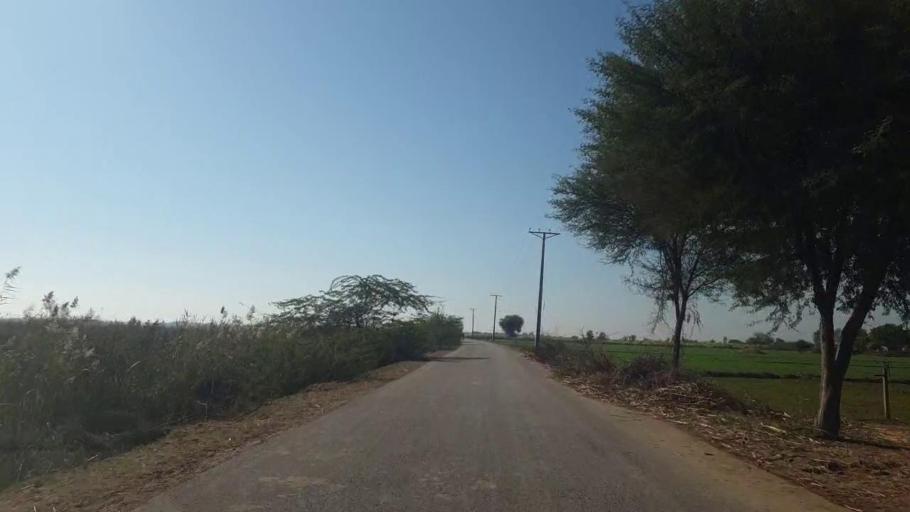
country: PK
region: Sindh
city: Kot Diji
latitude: 27.3098
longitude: 68.6474
